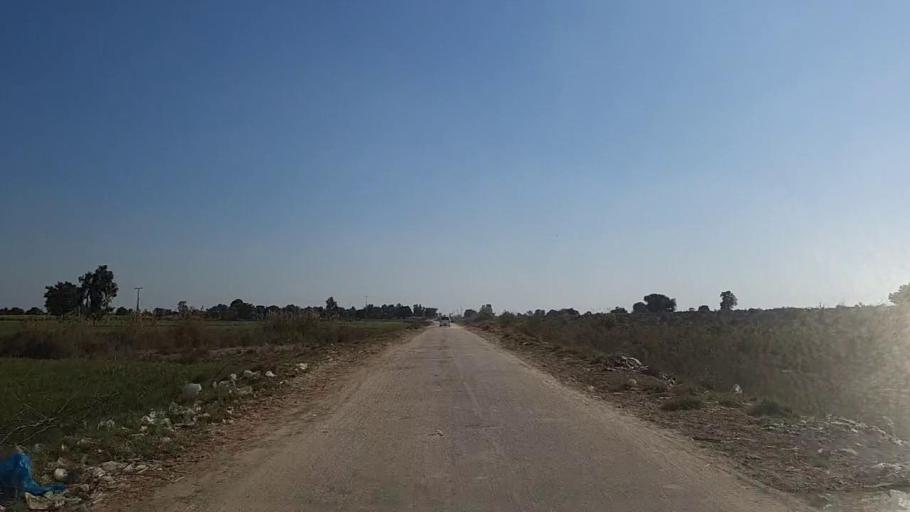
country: PK
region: Sindh
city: Nawabshah
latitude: 26.2353
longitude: 68.4256
